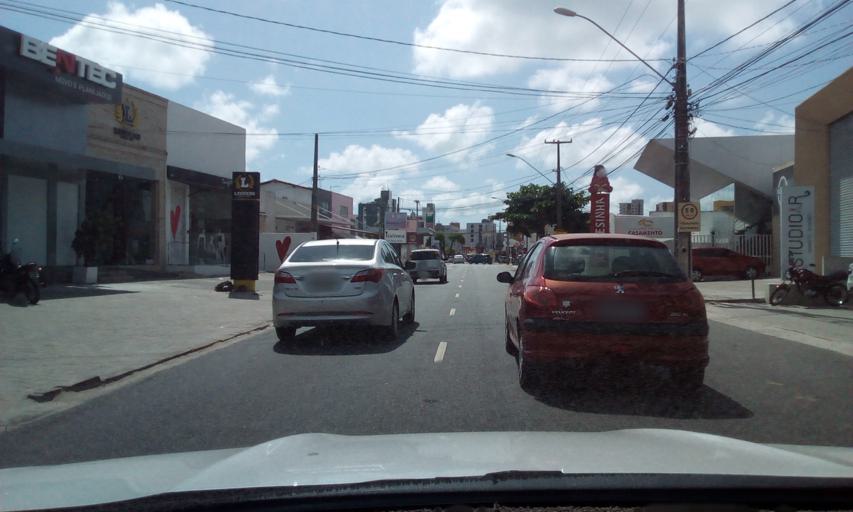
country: BR
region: Paraiba
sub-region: Joao Pessoa
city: Joao Pessoa
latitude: -7.1065
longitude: -34.8296
